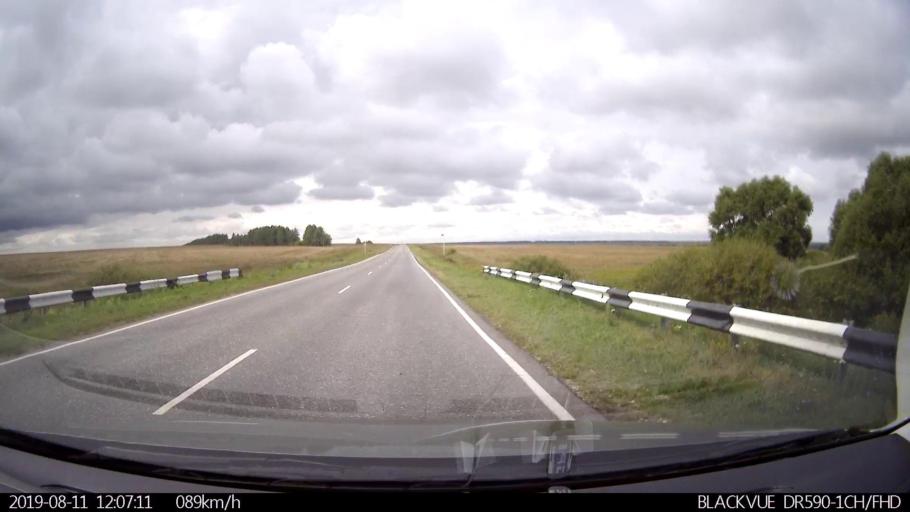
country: RU
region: Ulyanovsk
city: Silikatnyy
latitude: 53.9968
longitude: 48.1005
